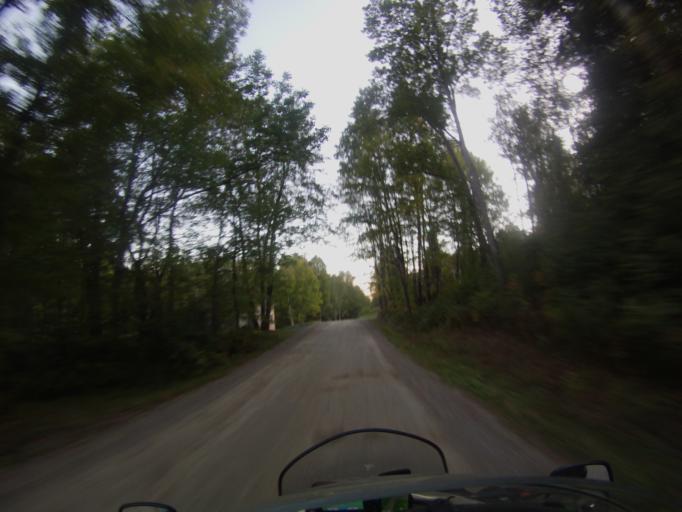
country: US
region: Vermont
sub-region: Addison County
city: Middlebury (village)
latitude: 44.0042
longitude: -73.0373
